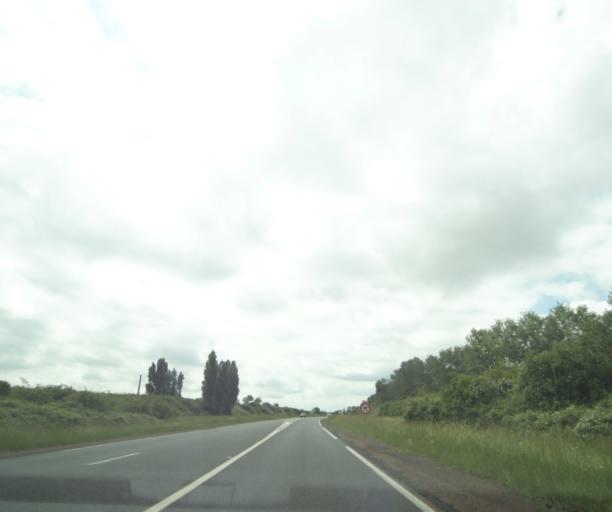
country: FR
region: Poitou-Charentes
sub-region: Departement des Deux-Sevres
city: Airvault
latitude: 46.8261
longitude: -0.2047
